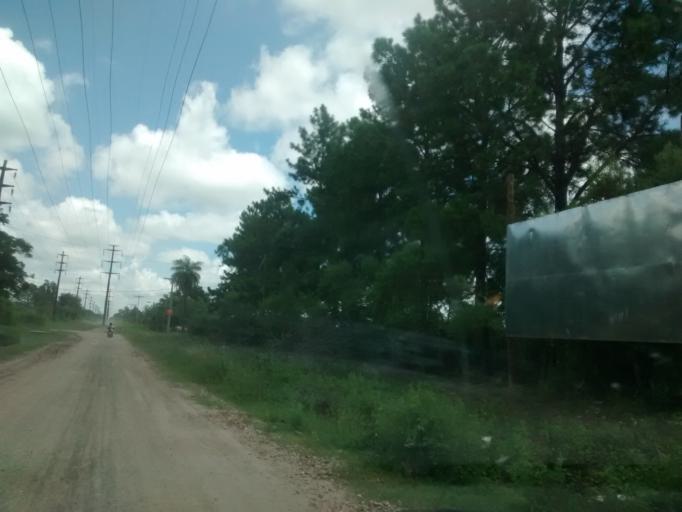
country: AR
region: Chaco
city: Fontana
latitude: -27.4174
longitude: -58.9816
